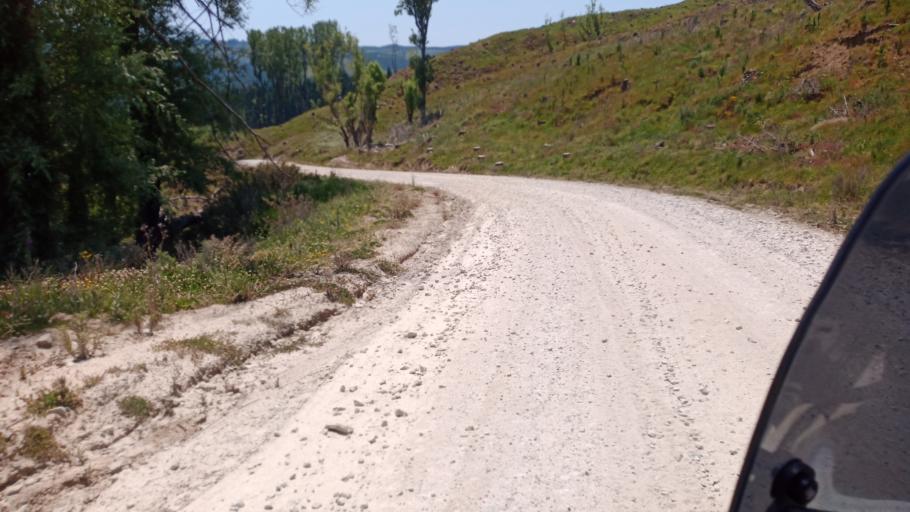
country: NZ
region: Gisborne
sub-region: Gisborne District
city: Gisborne
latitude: -38.2906
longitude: 178.0071
